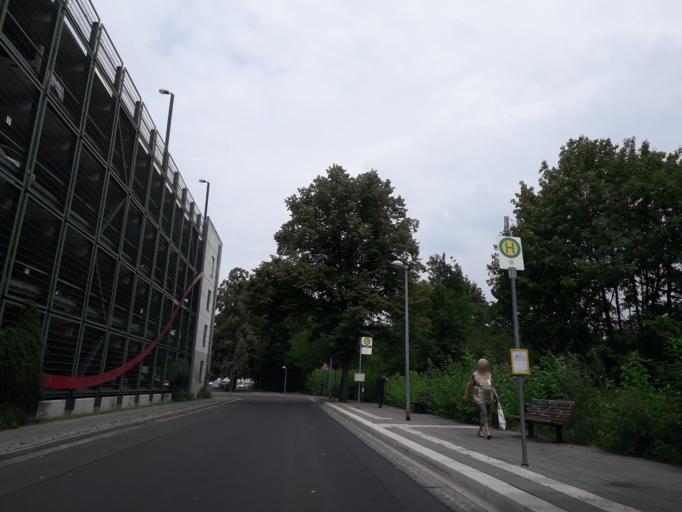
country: DE
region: Brandenburg
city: Hennigsdorf
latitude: 52.6389
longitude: 13.2046
